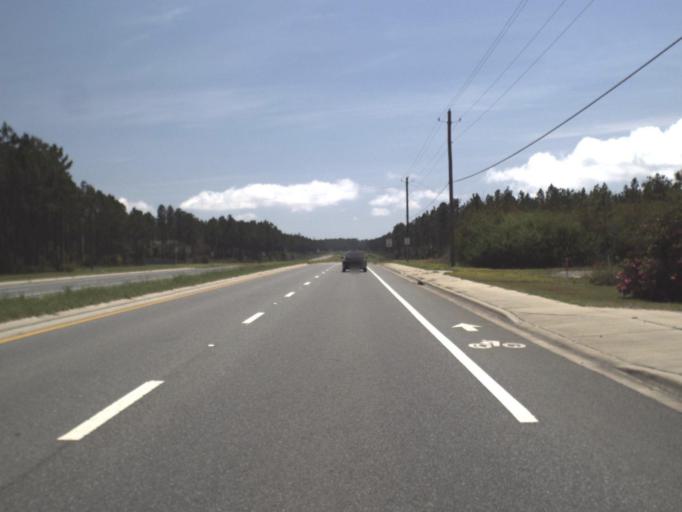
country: US
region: Florida
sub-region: Bay County
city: Laguna Beach
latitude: 30.3210
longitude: -85.8560
